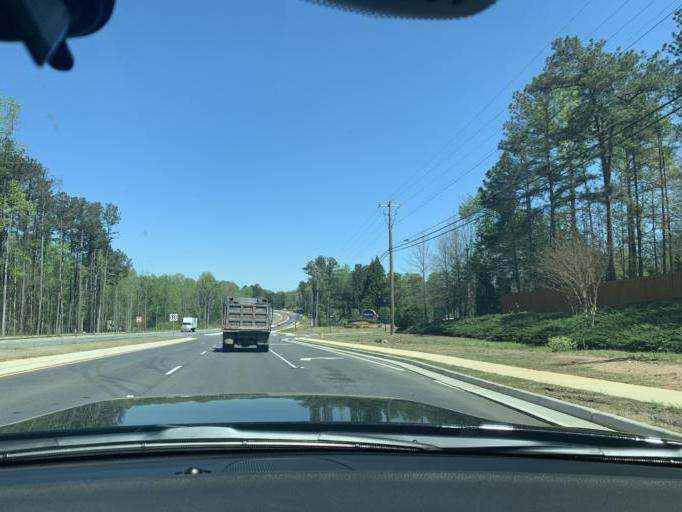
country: US
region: Georgia
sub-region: Forsyth County
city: Cumming
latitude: 34.2077
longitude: -84.1978
